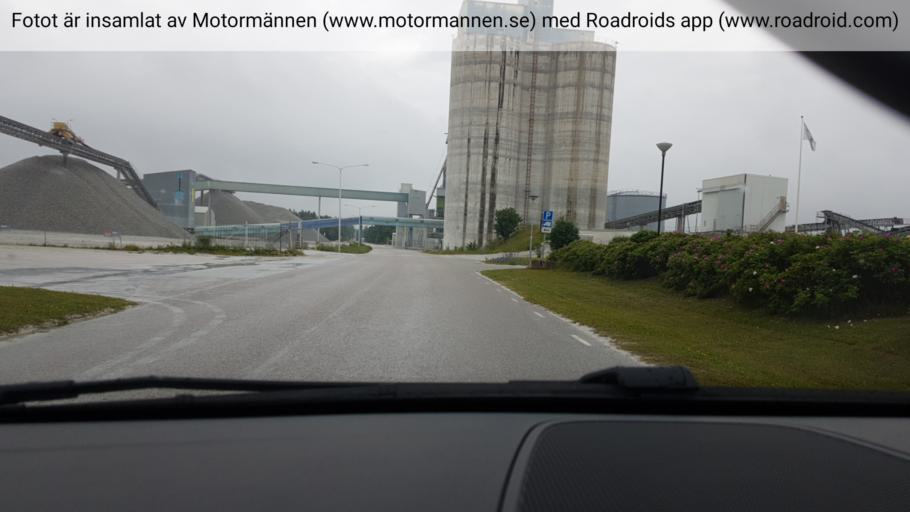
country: SE
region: Gotland
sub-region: Gotland
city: Slite
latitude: 57.8441
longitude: 18.8035
